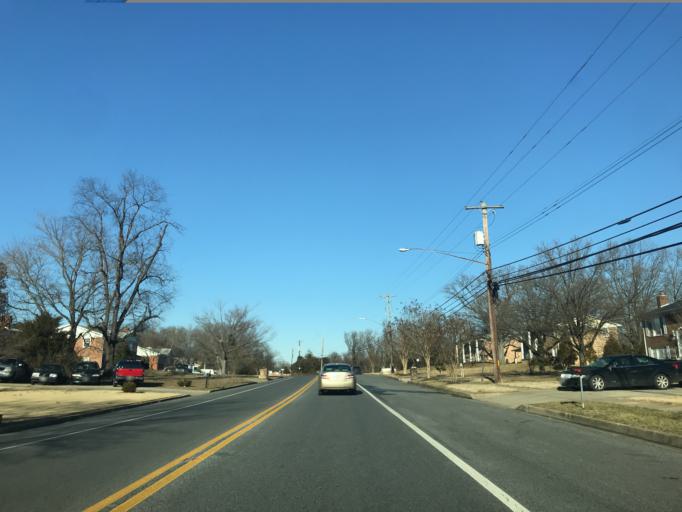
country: US
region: Maryland
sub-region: Prince George's County
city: Friendly
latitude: 38.7295
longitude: -76.9483
